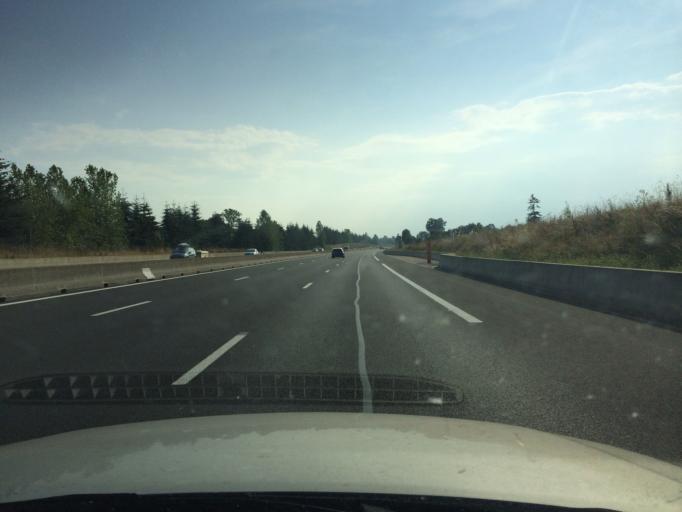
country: FR
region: Haute-Normandie
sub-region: Departement de l'Eure
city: Beuzeville
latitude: 49.3294
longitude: 0.3427
